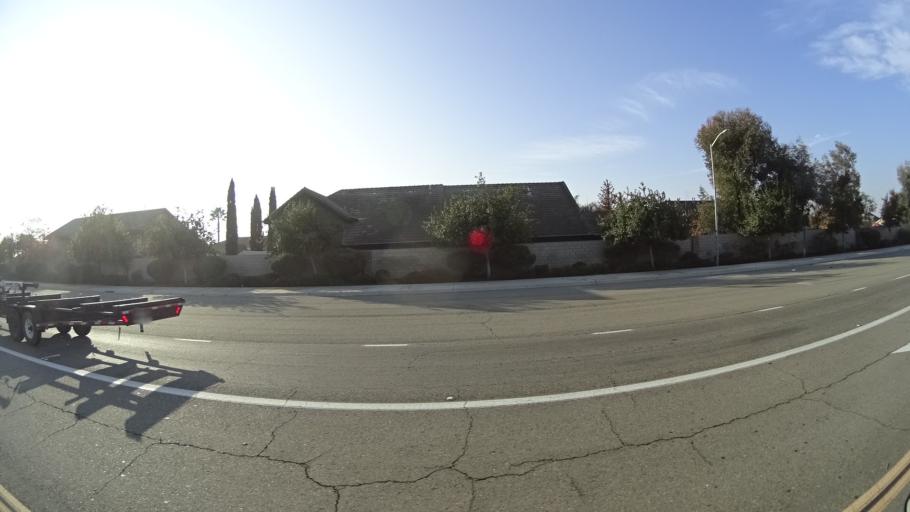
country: US
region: California
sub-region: Kern County
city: Rosedale
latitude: 35.3835
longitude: -119.1647
